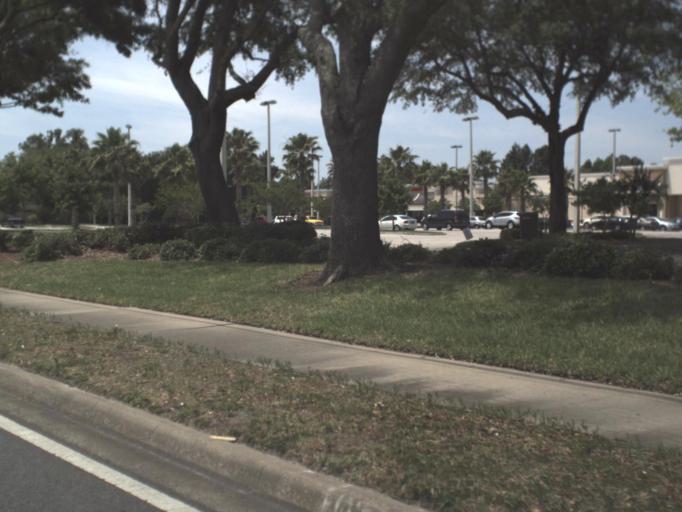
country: US
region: Florida
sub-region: Saint Johns County
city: Fruit Cove
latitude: 30.1492
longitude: -81.6327
